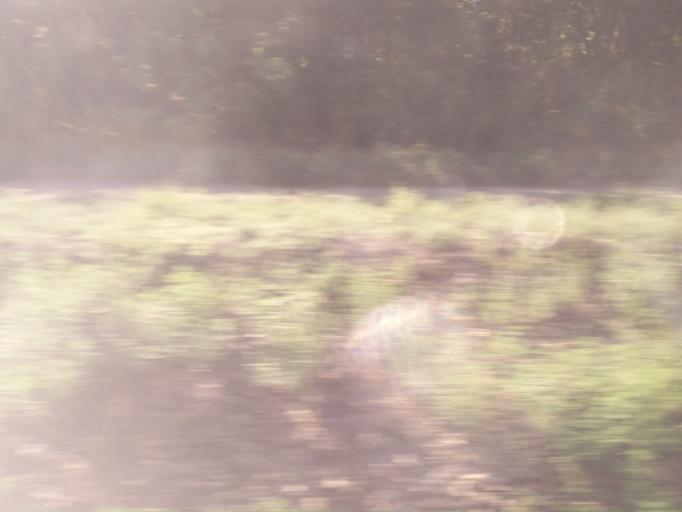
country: RU
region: Rostov
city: Gornyy
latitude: 47.8671
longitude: 40.1762
